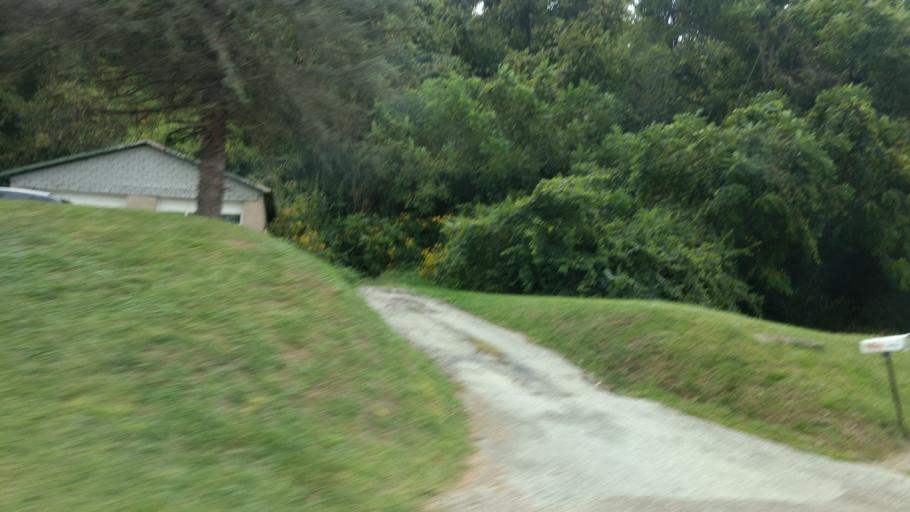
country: US
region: Pennsylvania
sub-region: Washington County
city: Wickerham Manor-Fisher
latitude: 40.1977
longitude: -79.8897
